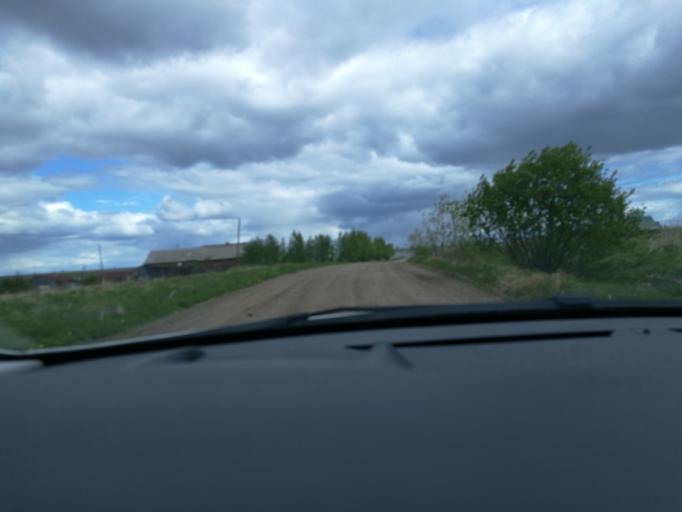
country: RU
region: Arkhangelskaya
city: Lukovetskiy
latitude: 64.2571
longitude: 41.8002
